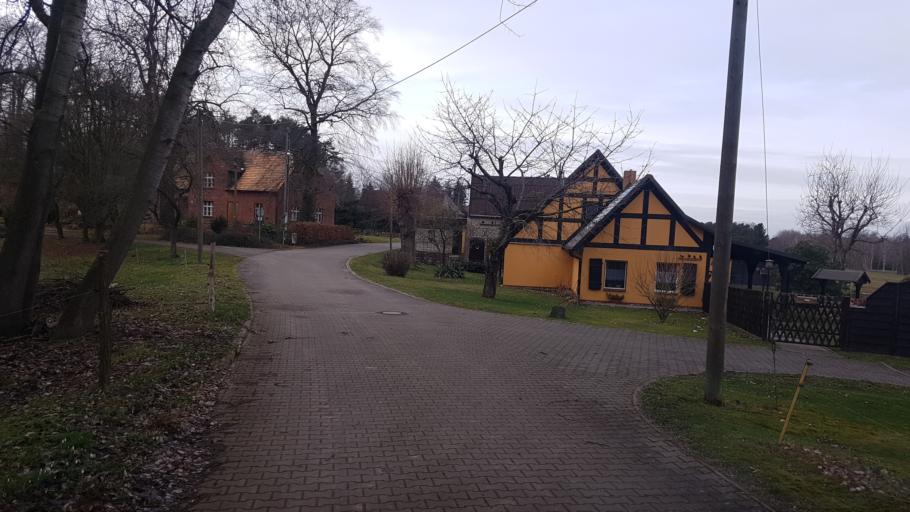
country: DE
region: Brandenburg
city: Crinitz
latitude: 51.7473
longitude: 13.7196
